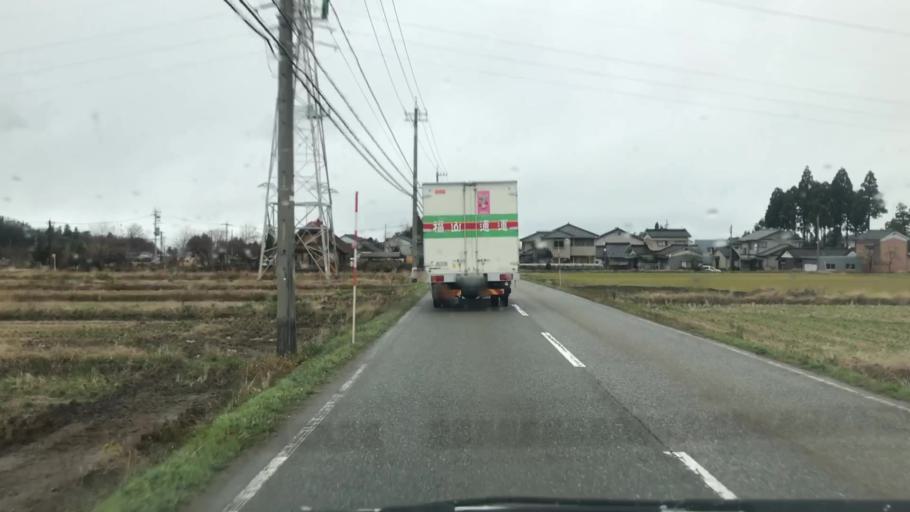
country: JP
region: Toyama
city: Kamiichi
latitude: 36.5988
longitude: 137.3234
